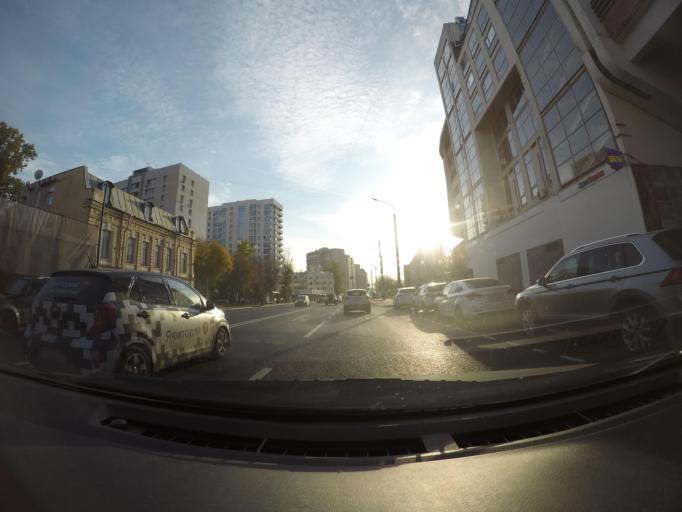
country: RU
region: Moscow
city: Lefortovo
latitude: 55.7785
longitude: 37.6909
